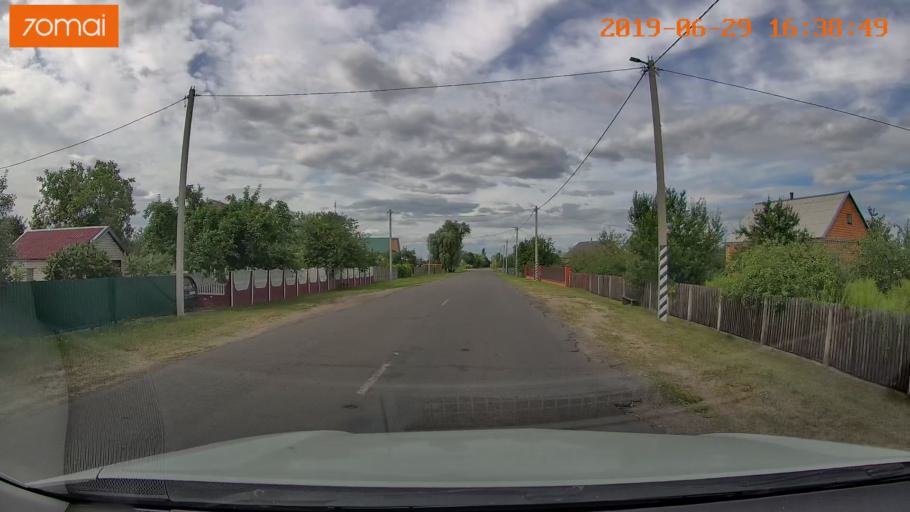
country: BY
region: Brest
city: Luninyets
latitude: 52.2359
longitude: 27.0154
